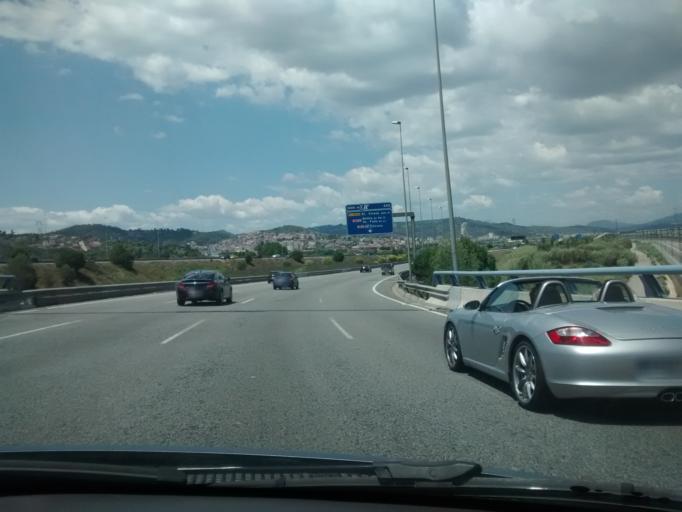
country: ES
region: Catalonia
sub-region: Provincia de Barcelona
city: Santa Coloma de Cervello
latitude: 41.3783
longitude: 2.0267
